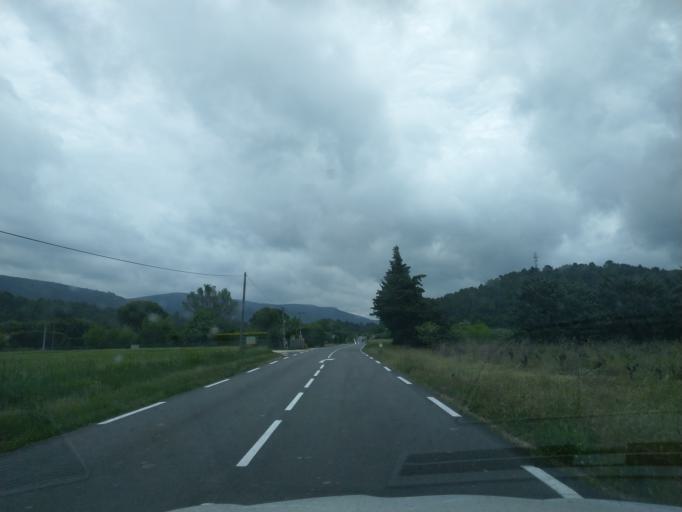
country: FR
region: Provence-Alpes-Cote d'Azur
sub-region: Departement du Var
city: Signes
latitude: 43.2846
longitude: 5.8381
